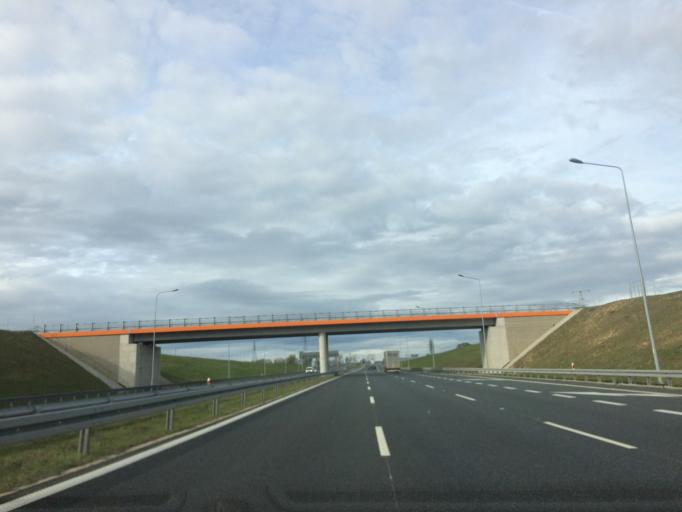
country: PL
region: Lower Silesian Voivodeship
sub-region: Legnica
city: Legnica
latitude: 51.1749
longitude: 16.0927
